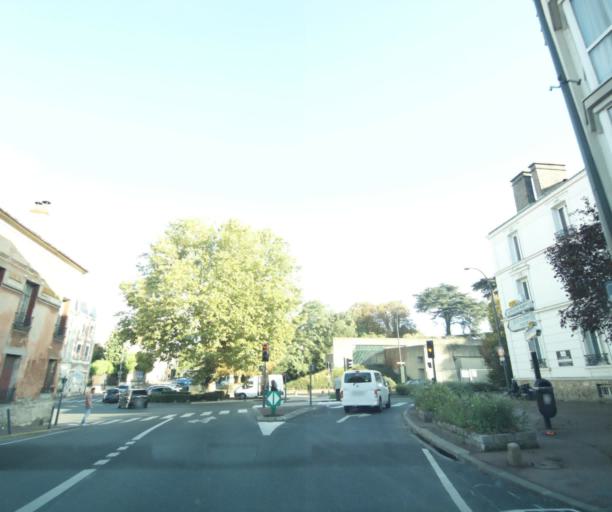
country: FR
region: Ile-de-France
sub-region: Departement des Hauts-de-Seine
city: Chatillon
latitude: 48.7999
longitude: 2.2852
